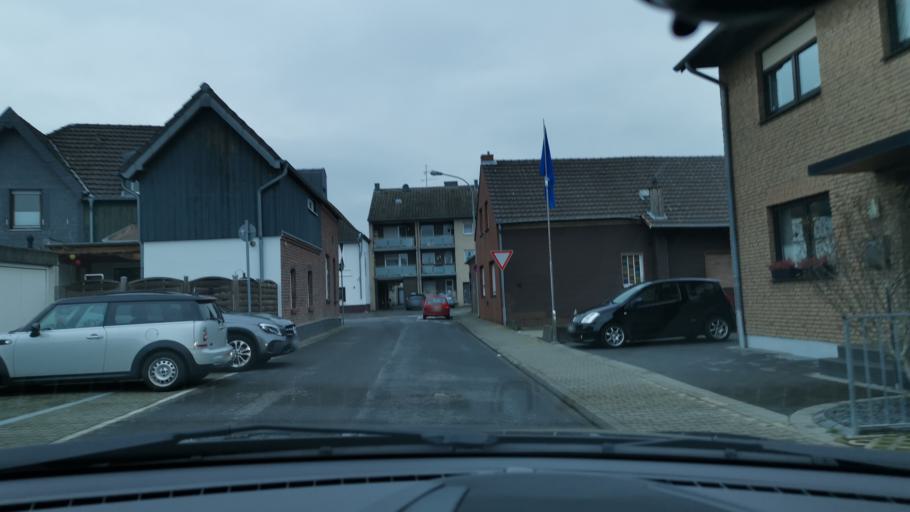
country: DE
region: North Rhine-Westphalia
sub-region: Regierungsbezirk Dusseldorf
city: Neubrueck
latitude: 51.1295
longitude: 6.6285
